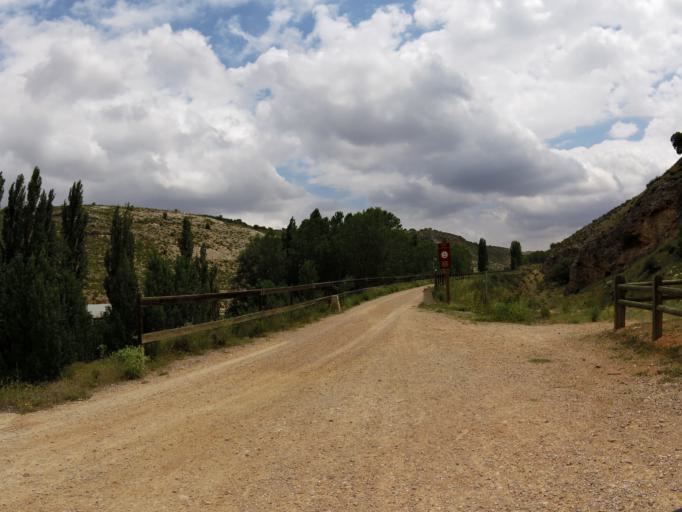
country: ES
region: Castille-La Mancha
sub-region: Provincia de Albacete
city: Casas de Lazaro
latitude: 38.8097
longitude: -2.3199
